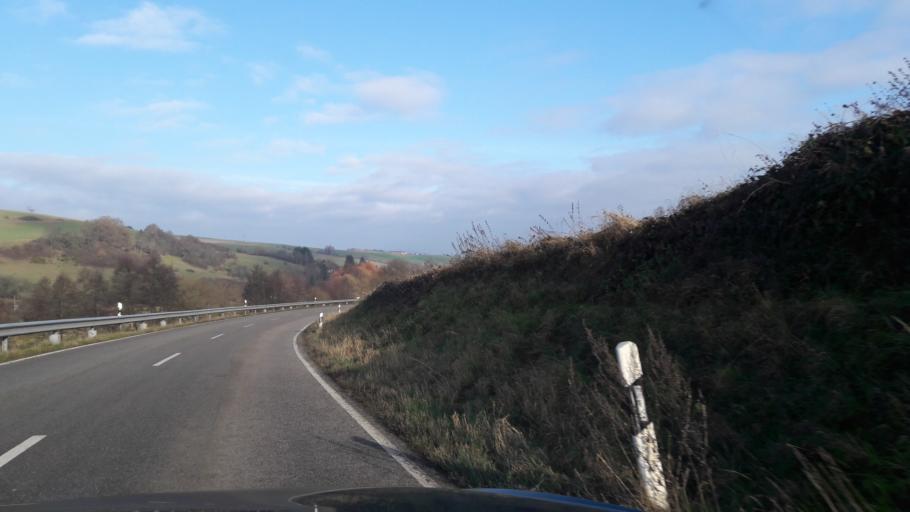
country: DE
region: Rheinland-Pfalz
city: Borsborn
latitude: 49.4600
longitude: 7.3969
